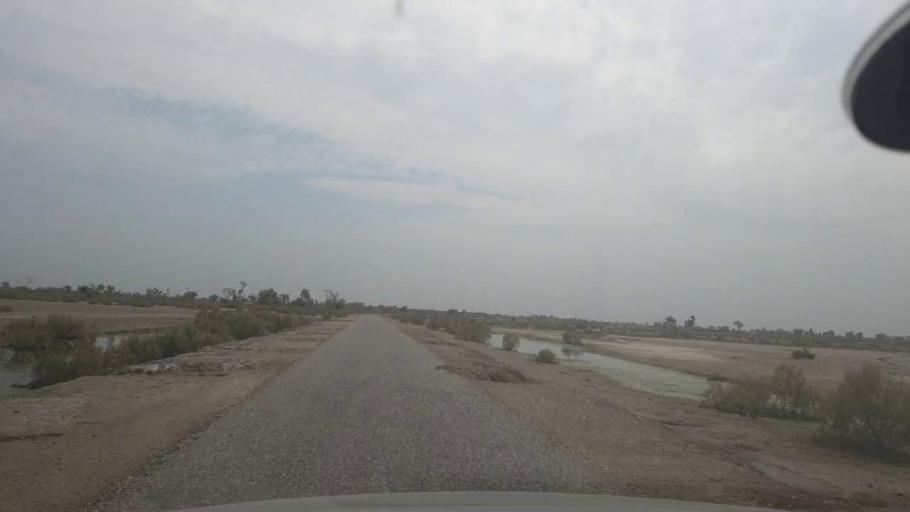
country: PK
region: Balochistan
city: Mehrabpur
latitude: 28.0581
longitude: 68.1376
